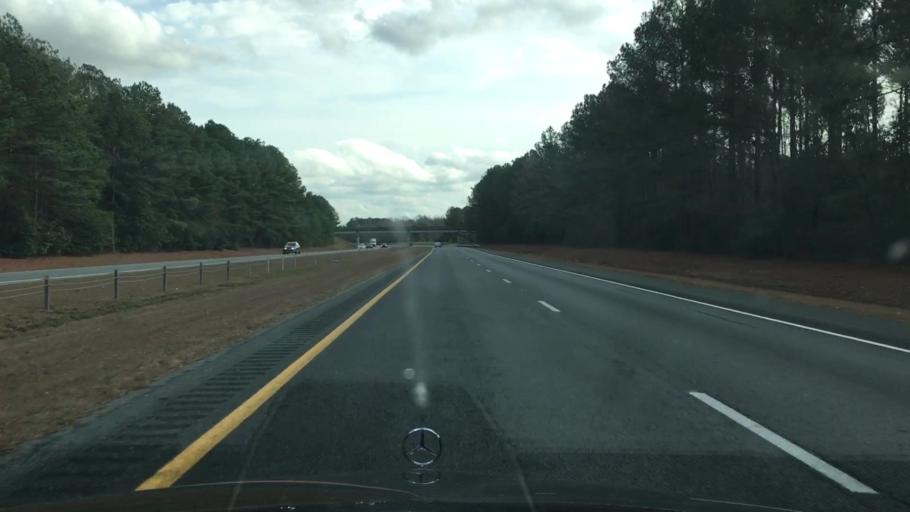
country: US
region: North Carolina
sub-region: Sampson County
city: Clinton
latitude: 35.2163
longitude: -78.3313
